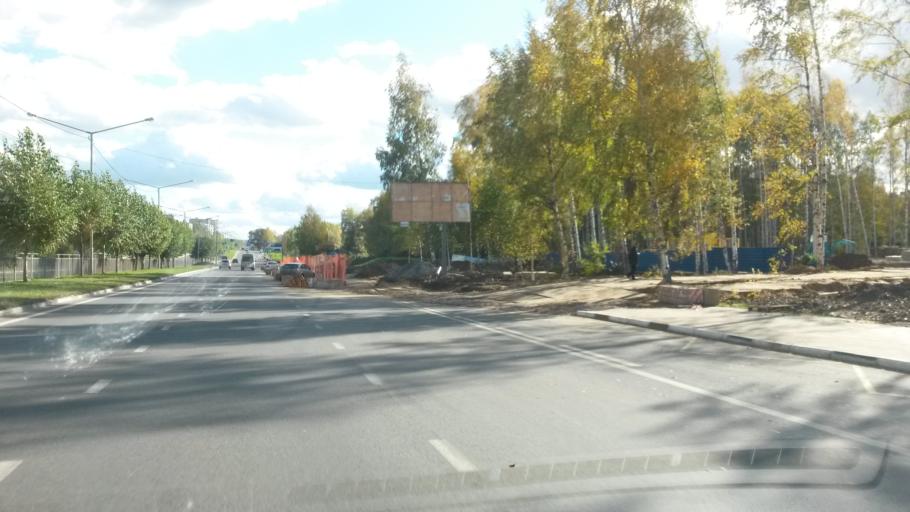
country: RU
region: Jaroslavl
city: Yaroslavl
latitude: 57.5769
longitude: 39.9160
